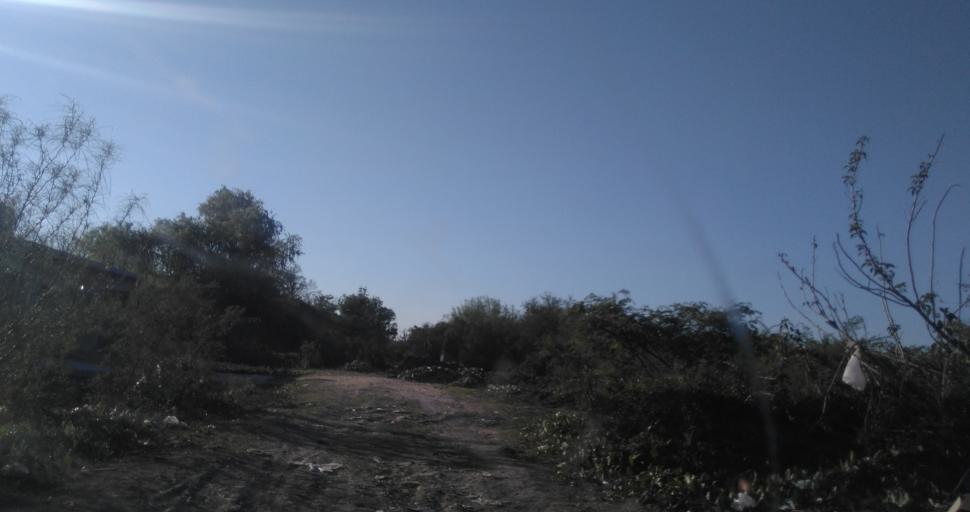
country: AR
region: Chaco
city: Resistencia
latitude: -27.4886
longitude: -59.0018
